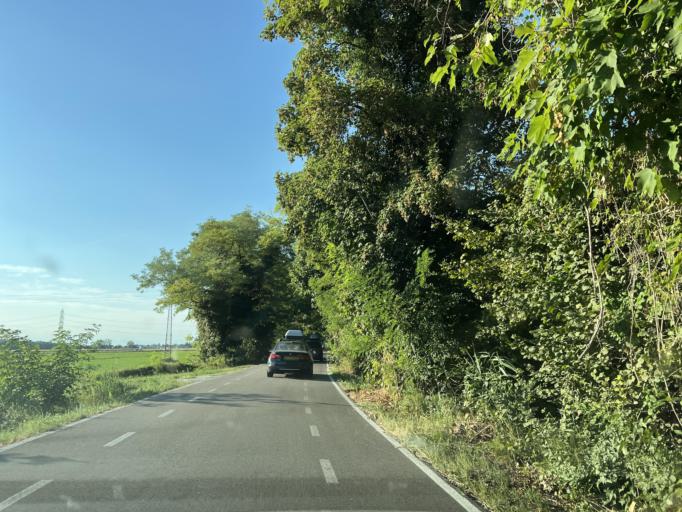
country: IT
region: Friuli Venezia Giulia
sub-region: Provincia di Gorizia
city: San Canzian d'Isonzo
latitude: 45.7783
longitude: 13.4758
